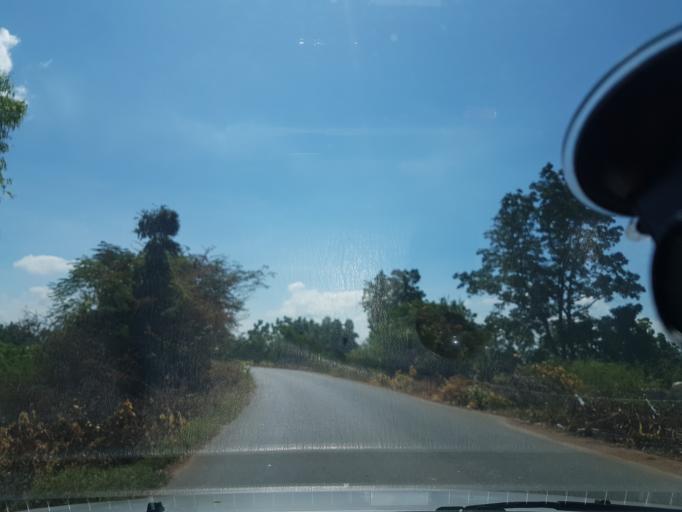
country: TH
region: Lop Buri
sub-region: Amphoe Tha Luang
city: Tha Luang
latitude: 14.9976
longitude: 101.0107
